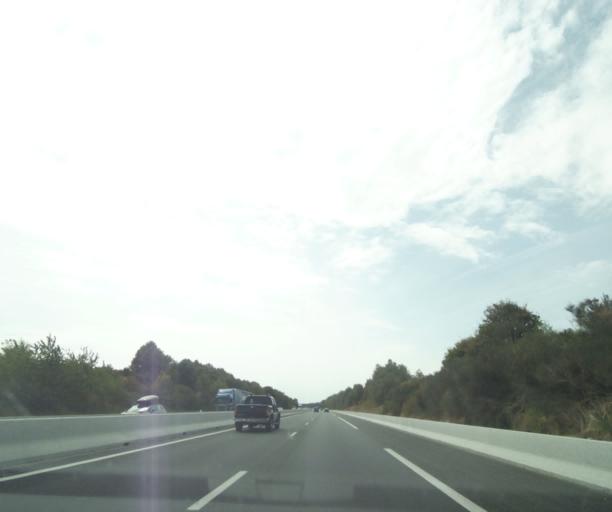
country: FR
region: Poitou-Charentes
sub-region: Departement des Deux-Sevres
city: Beauvoir-sur-Niort
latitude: 46.2015
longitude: -0.4760
